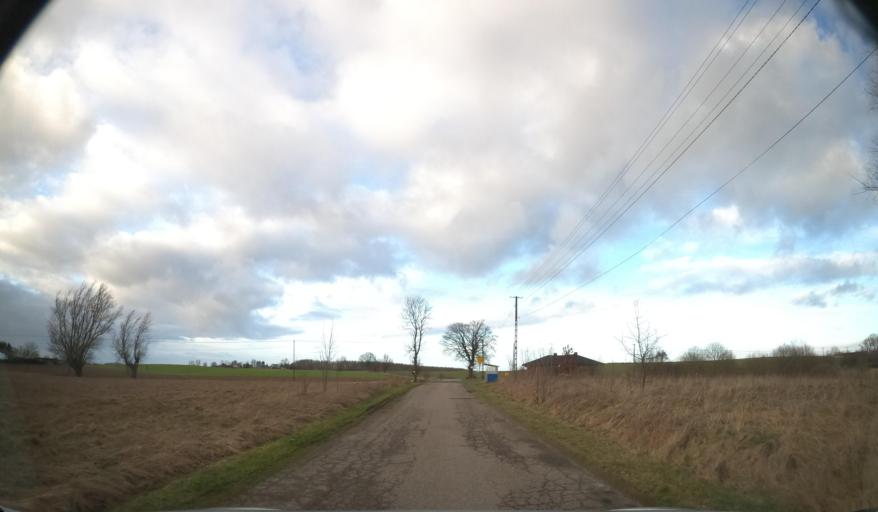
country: PL
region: West Pomeranian Voivodeship
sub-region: Powiat koszalinski
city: Mielno
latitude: 54.1708
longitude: 16.0363
